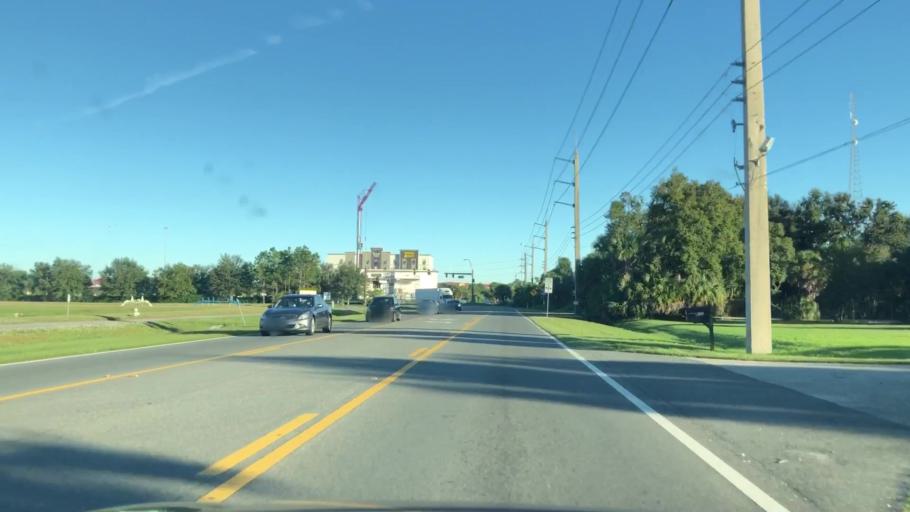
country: US
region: Florida
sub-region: Sarasota County
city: Fruitville
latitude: 27.3342
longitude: -82.4493
